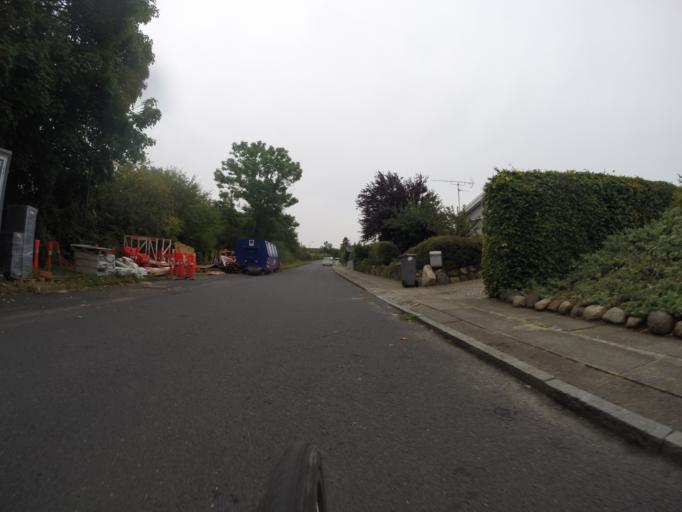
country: DK
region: Capital Region
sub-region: Herlev Kommune
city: Herlev
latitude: 55.7466
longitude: 12.4273
